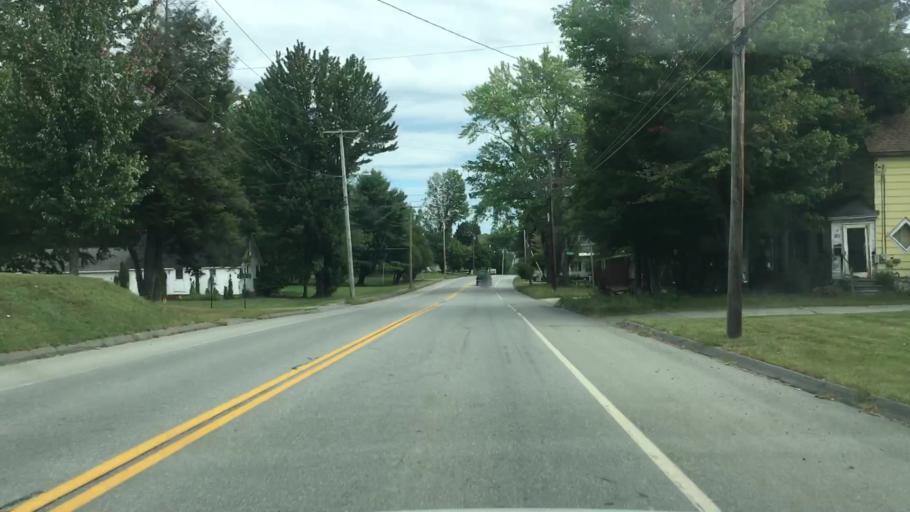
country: US
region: Maine
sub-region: Piscataquis County
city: Milo
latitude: 45.2484
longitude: -68.9974
